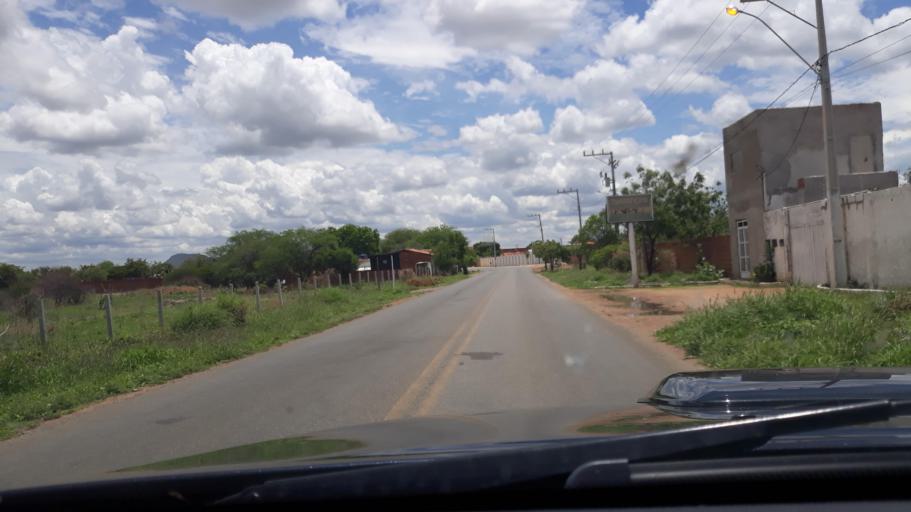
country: BR
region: Bahia
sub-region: Guanambi
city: Guanambi
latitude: -14.1994
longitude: -42.7938
